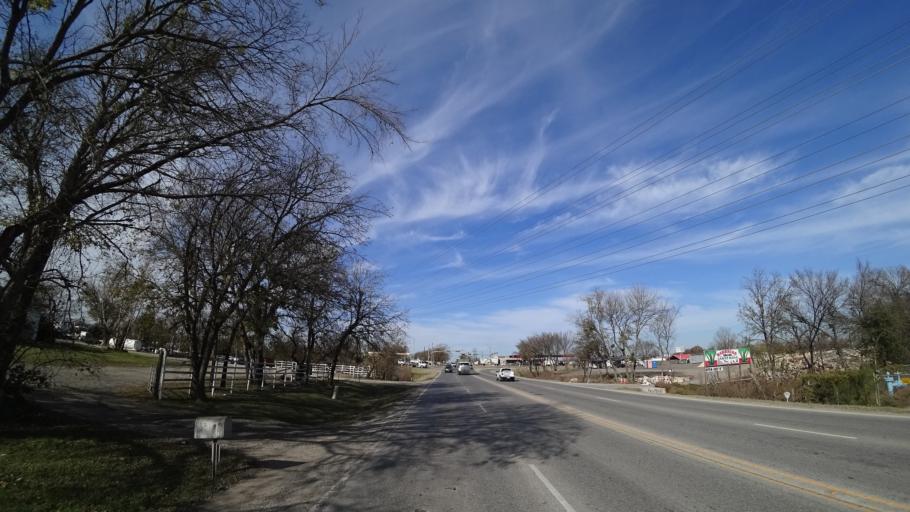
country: US
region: Texas
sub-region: Travis County
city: Onion Creek
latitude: 30.1634
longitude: -97.6915
